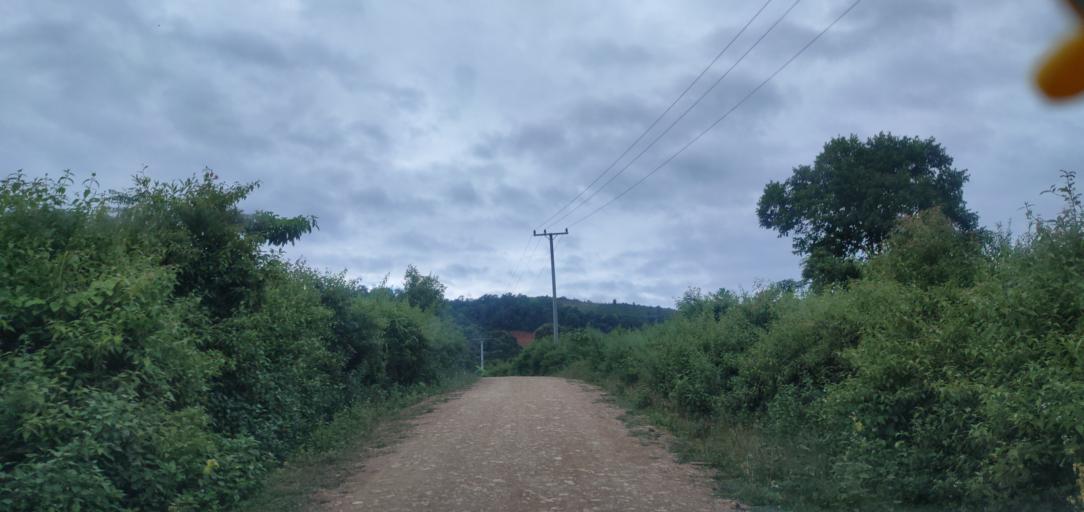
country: LA
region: Phongsali
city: Khoa
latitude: 21.1941
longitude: 102.2945
